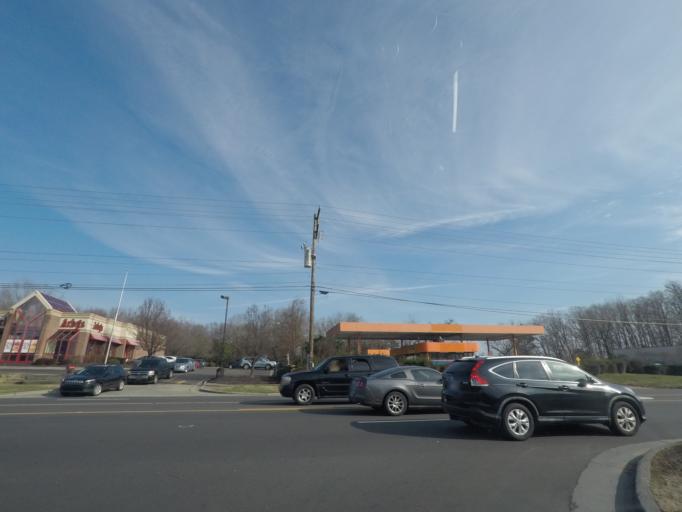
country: US
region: North Carolina
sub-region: Durham County
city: Durham
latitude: 36.0762
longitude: -78.9099
